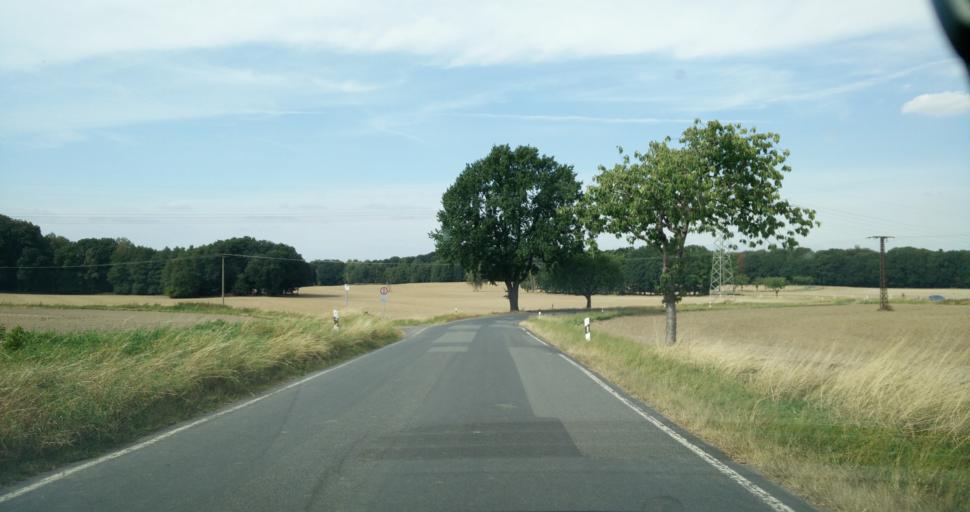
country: DE
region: Saxony
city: Bad Lausick
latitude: 51.1433
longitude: 12.6872
